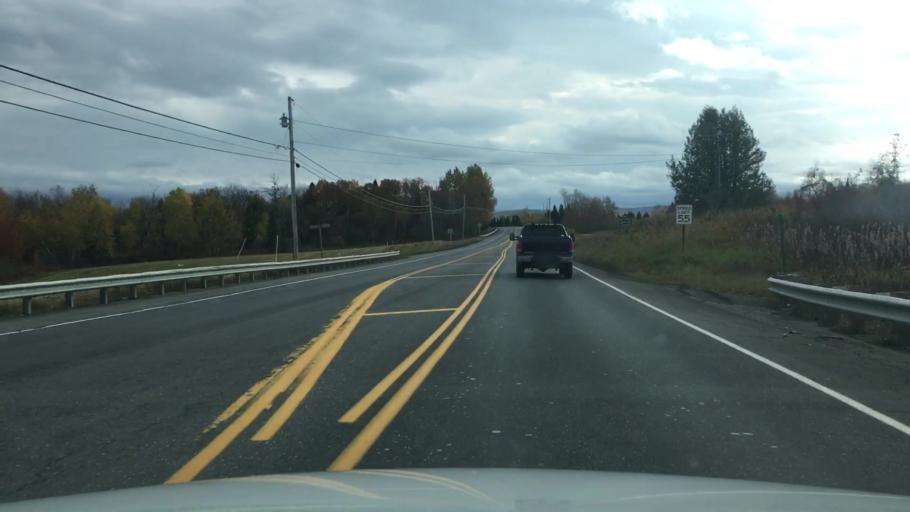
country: US
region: Maine
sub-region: Aroostook County
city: Easton
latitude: 46.5678
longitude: -67.9497
